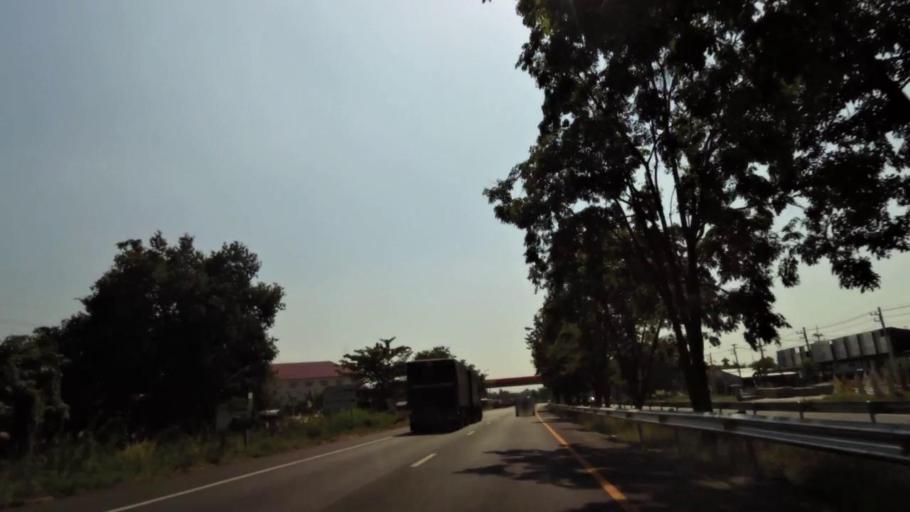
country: TH
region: Nakhon Sawan
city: Kao Liao
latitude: 15.9625
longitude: 100.1195
